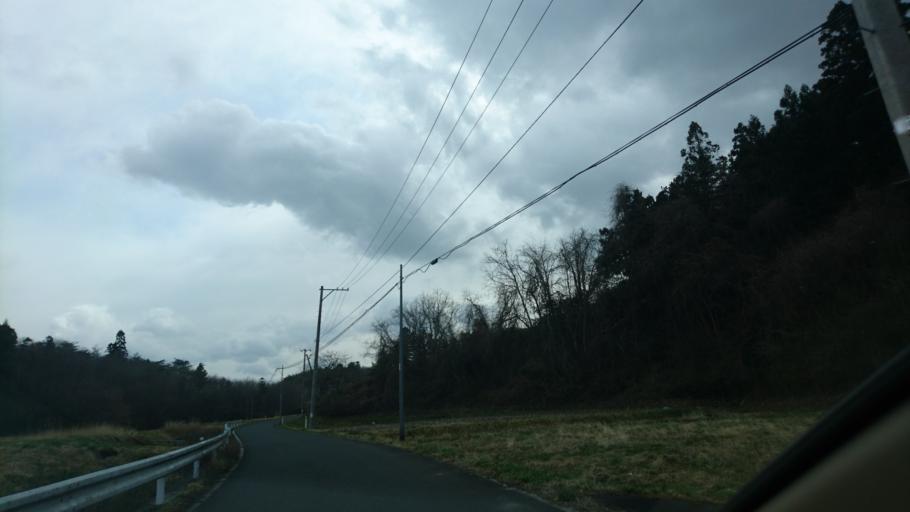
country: JP
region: Iwate
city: Ichinoseki
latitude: 38.8874
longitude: 141.1688
